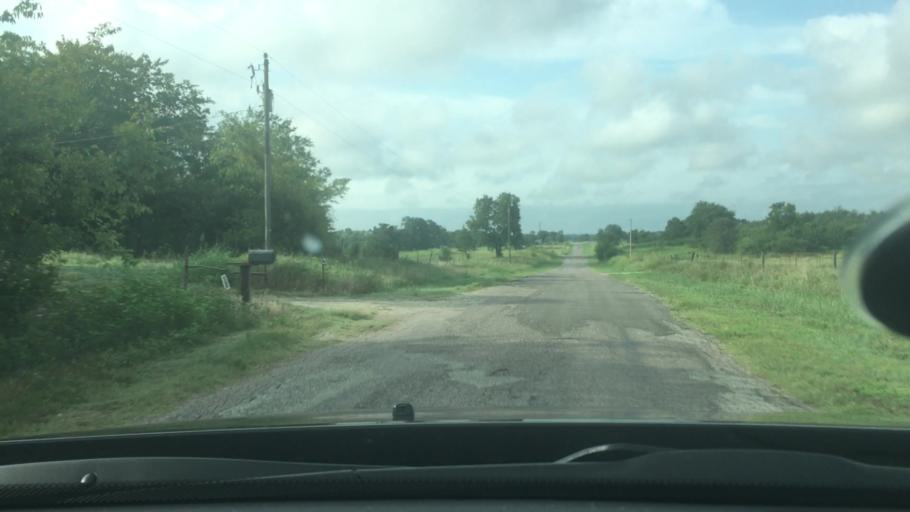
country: US
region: Oklahoma
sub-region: Pontotoc County
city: Ada
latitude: 34.6906
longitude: -96.5298
